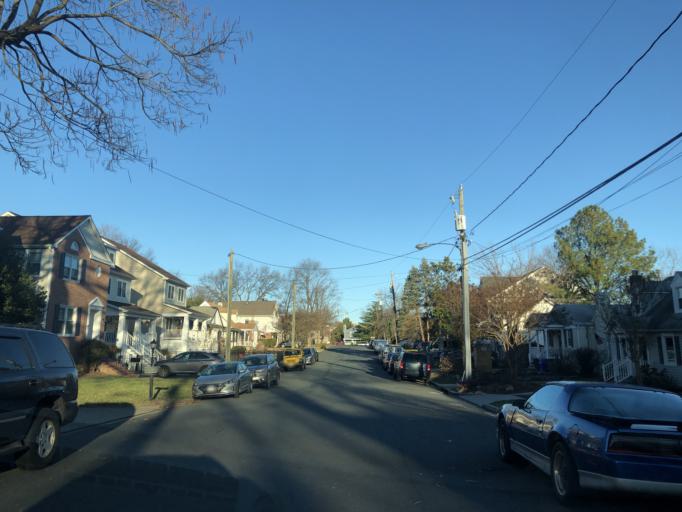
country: US
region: Virginia
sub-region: Fairfax County
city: Baileys Crossroads
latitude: 38.8744
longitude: -77.1297
